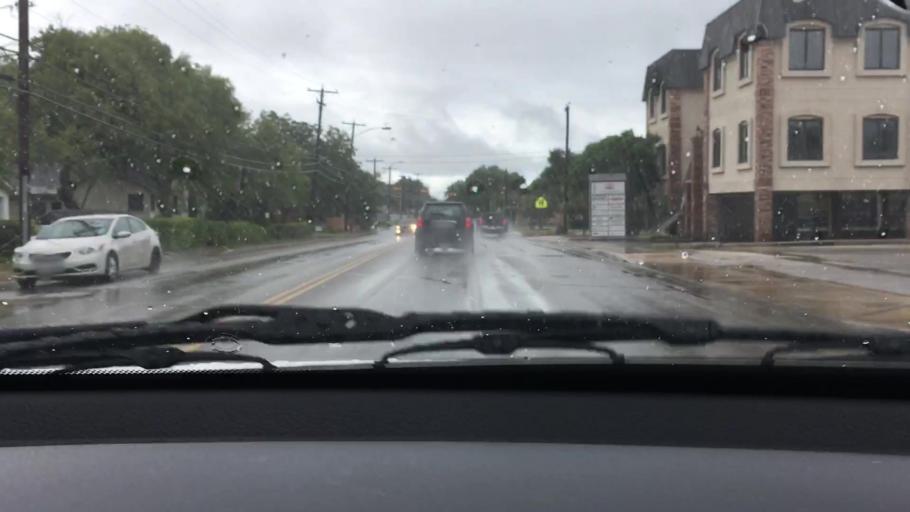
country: US
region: Texas
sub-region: Bexar County
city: Alamo Heights
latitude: 29.4936
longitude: -98.4666
